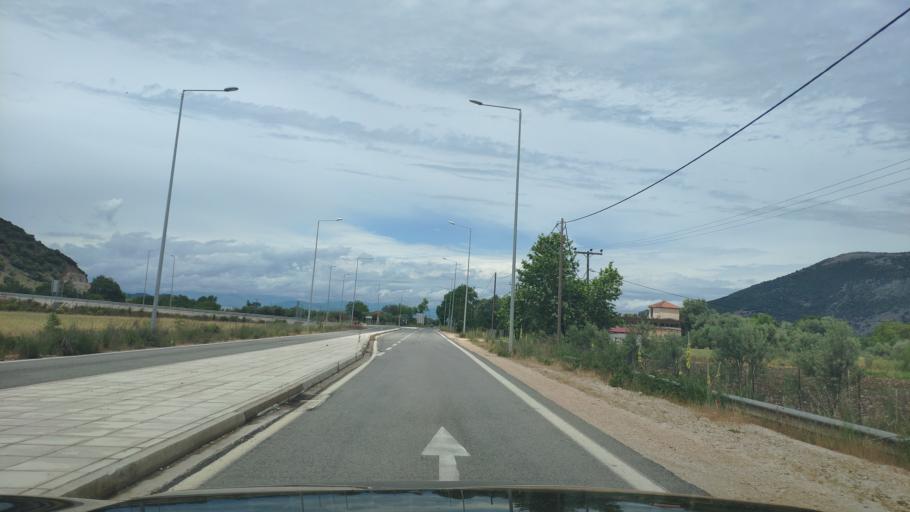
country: GR
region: West Greece
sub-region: Nomos Aitolias kai Akarnanias
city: Vonitsa
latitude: 38.8913
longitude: 20.9001
